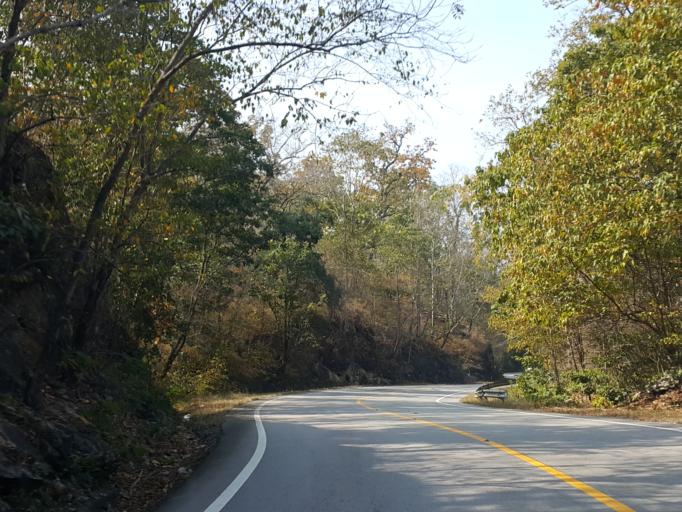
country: TH
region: Chiang Mai
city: Hot
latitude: 18.2298
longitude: 98.5117
